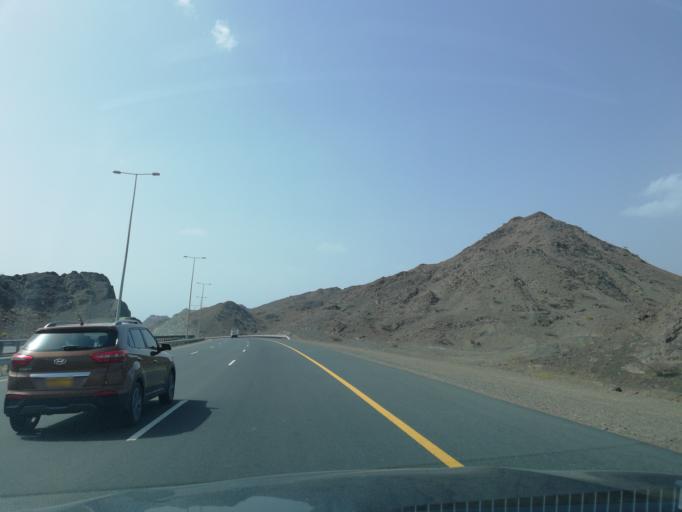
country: OM
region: Ash Sharqiyah
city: Ibra'
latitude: 22.9637
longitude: 58.2453
